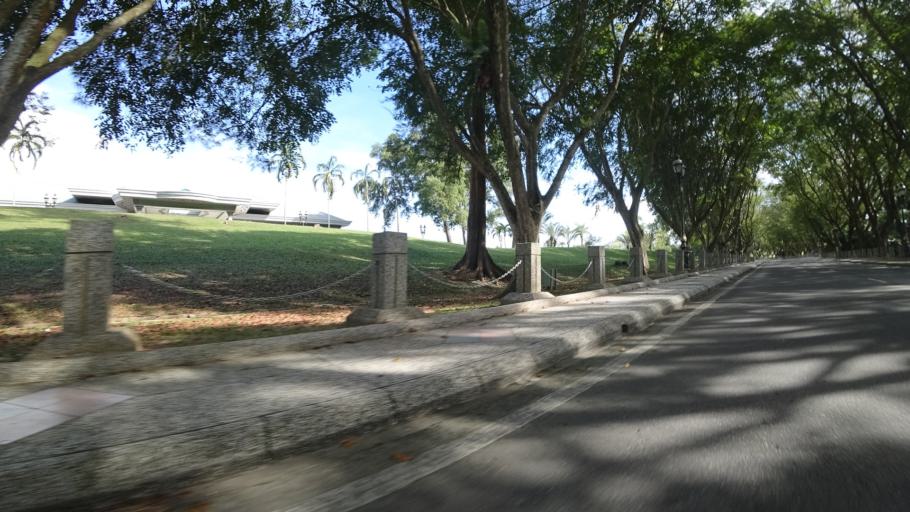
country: BN
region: Brunei and Muara
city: Bandar Seri Begawan
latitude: 4.9439
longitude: 114.8335
